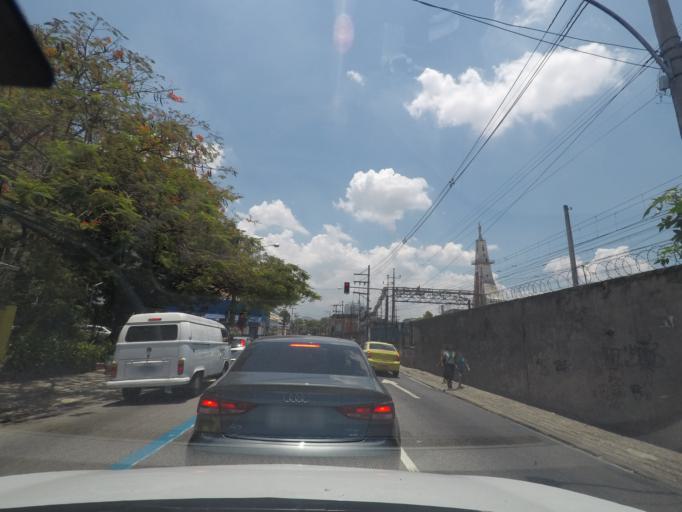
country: BR
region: Rio de Janeiro
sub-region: Rio De Janeiro
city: Rio de Janeiro
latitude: -22.9024
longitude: -43.2650
